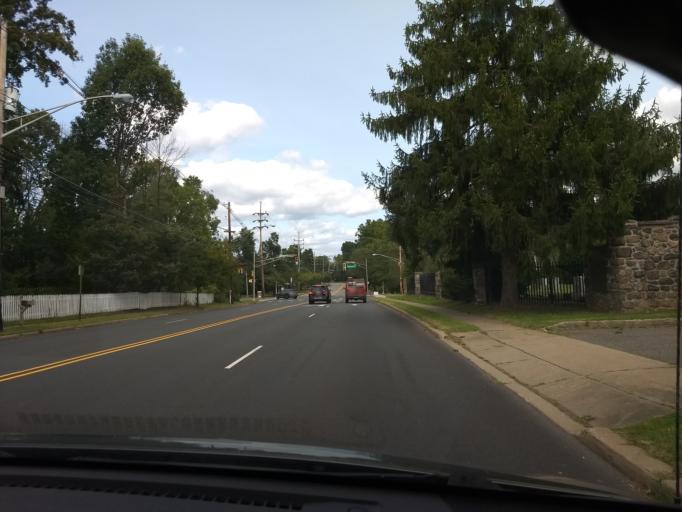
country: US
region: New Jersey
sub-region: Morris County
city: Morris Plains
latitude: 40.8279
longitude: -74.4468
